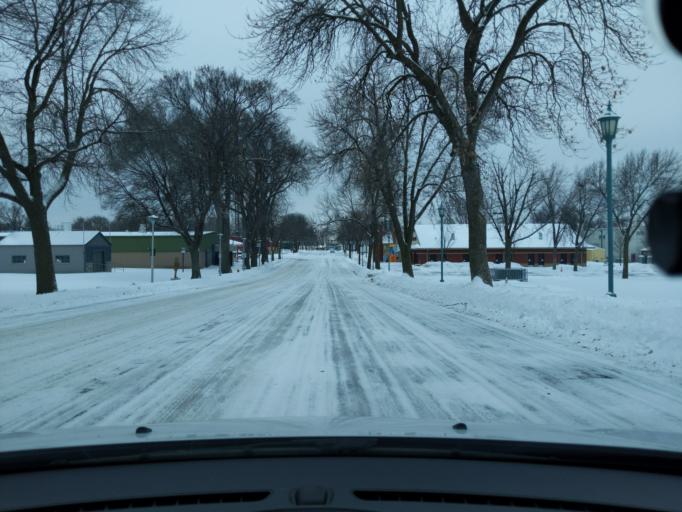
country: US
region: Minnesota
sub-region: Ramsey County
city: Falcon Heights
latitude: 44.9827
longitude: -93.1692
